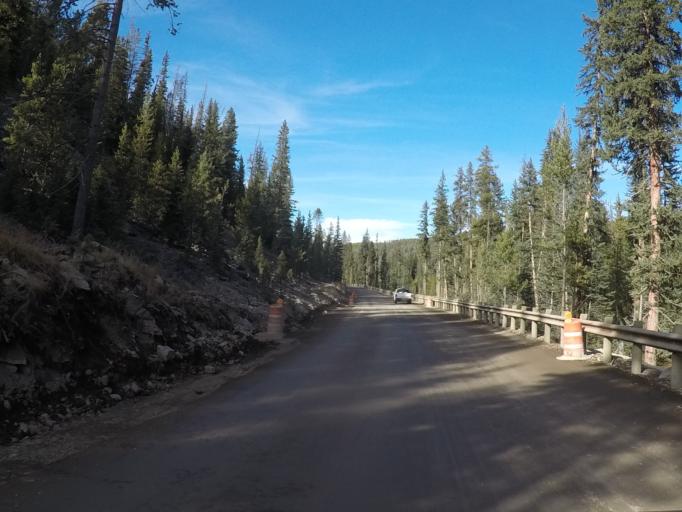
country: US
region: Montana
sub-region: Gallatin County
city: West Yellowstone
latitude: 44.8298
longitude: -110.7279
